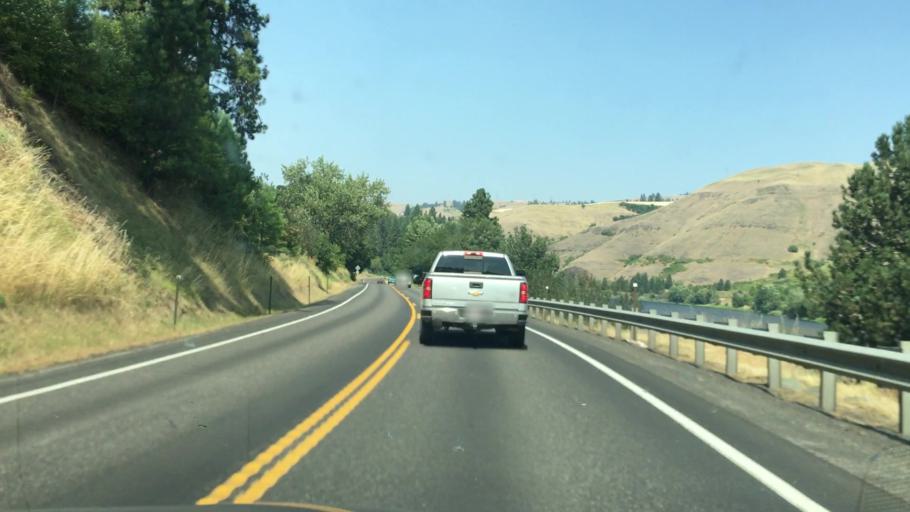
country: US
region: Idaho
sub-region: Clearwater County
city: Orofino
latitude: 46.5015
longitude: -116.5024
